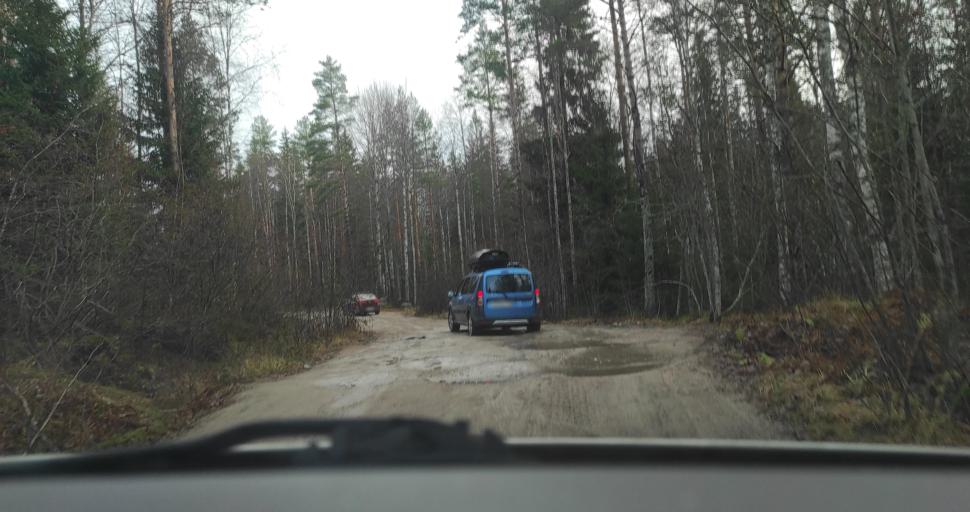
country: RU
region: Republic of Karelia
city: Pitkyaranta
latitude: 61.7374
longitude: 31.3885
